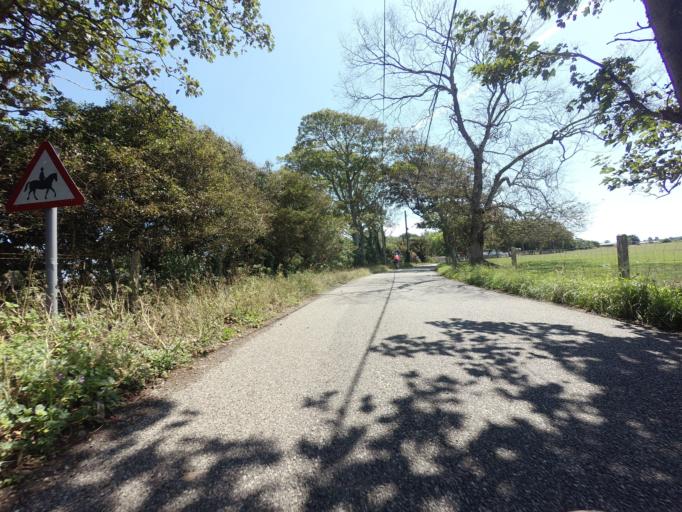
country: GB
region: England
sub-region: Kent
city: Lydd
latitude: 50.9582
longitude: 0.9040
